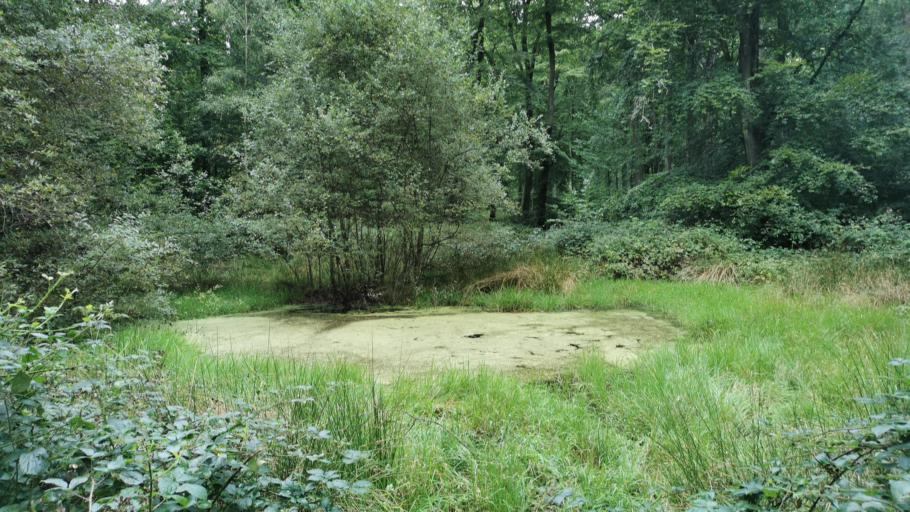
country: FR
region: Haute-Normandie
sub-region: Departement de la Seine-Maritime
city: Martin-Eglise
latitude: 49.8899
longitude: 1.1731
